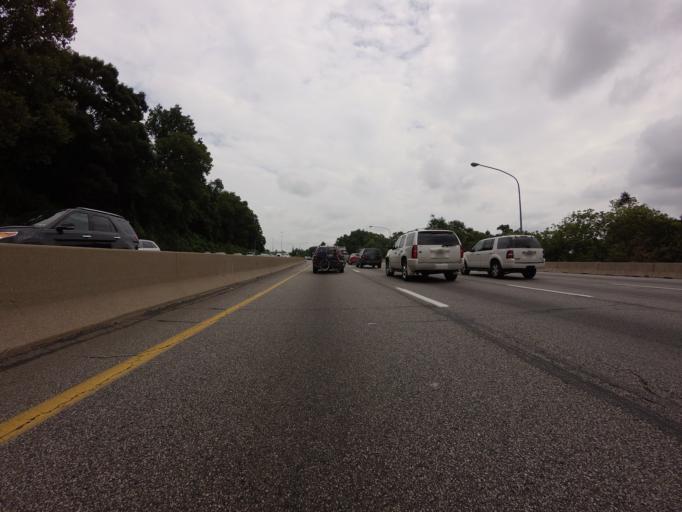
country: US
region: Pennsylvania
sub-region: Montgomery County
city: Bala-Cynwyd
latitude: 39.9996
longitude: -75.1952
